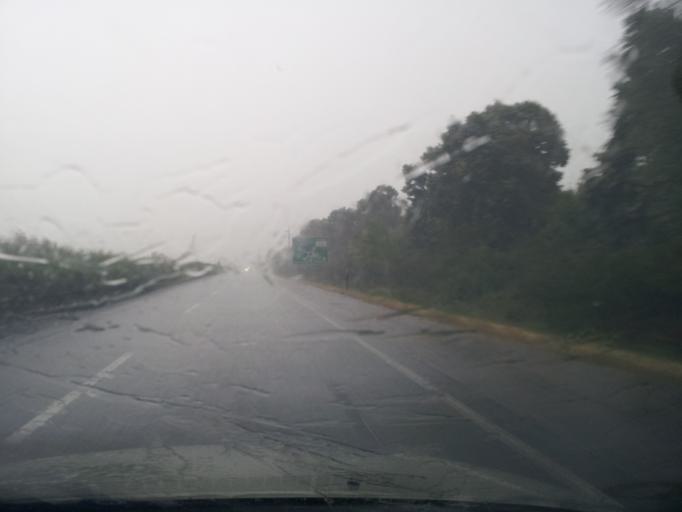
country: HU
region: Borsod-Abauj-Zemplen
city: Felsozsolca
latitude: 48.1138
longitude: 20.8649
